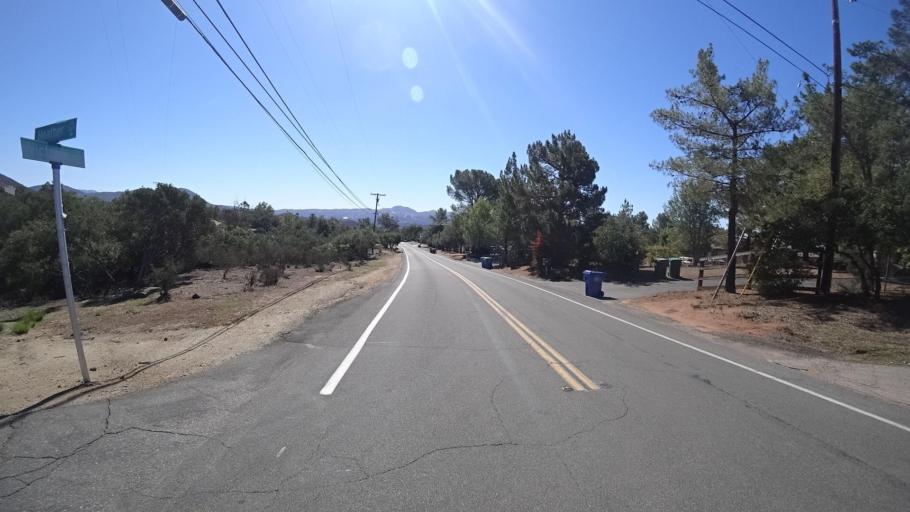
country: US
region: California
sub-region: San Diego County
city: Alpine
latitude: 32.8448
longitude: -116.7479
